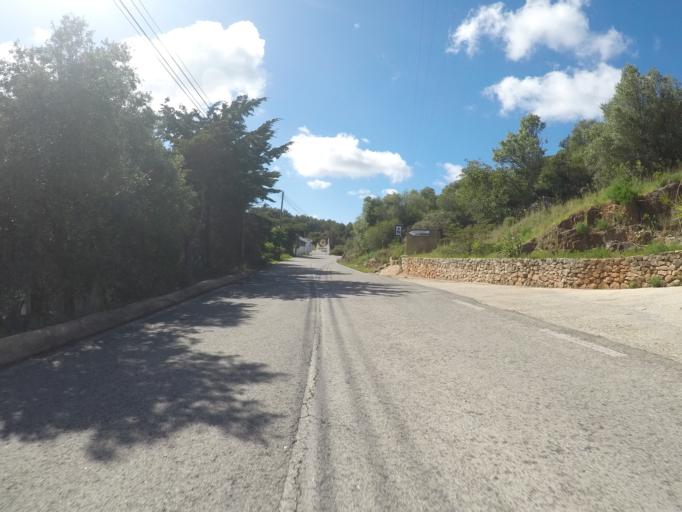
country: PT
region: Faro
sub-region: Vila do Bispo
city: Vila do Bispo
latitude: 37.0750
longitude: -8.8306
